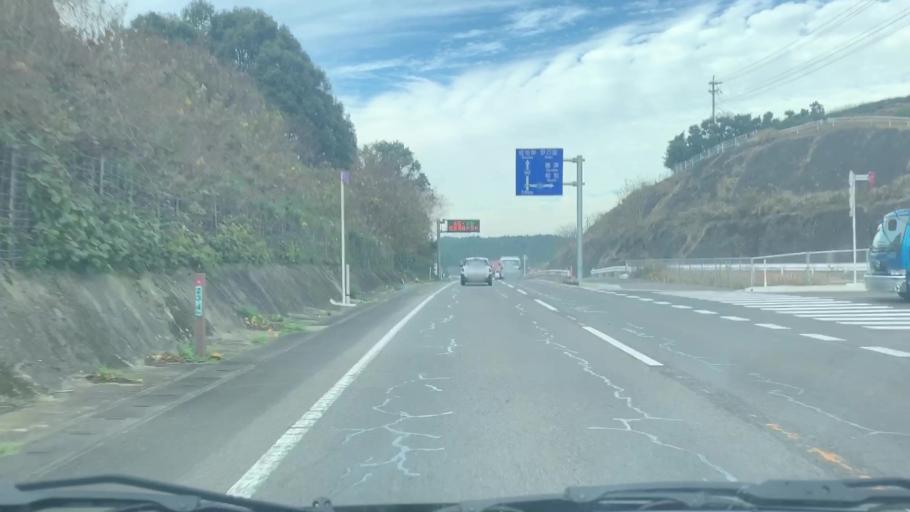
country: JP
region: Saga Prefecture
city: Takeocho-takeo
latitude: 33.2628
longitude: 129.9692
